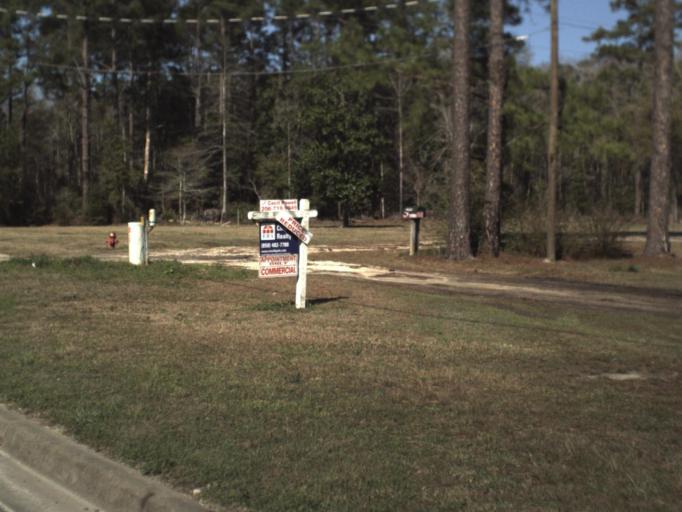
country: US
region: Florida
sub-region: Jackson County
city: Marianna
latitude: 30.7426
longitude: -85.1861
